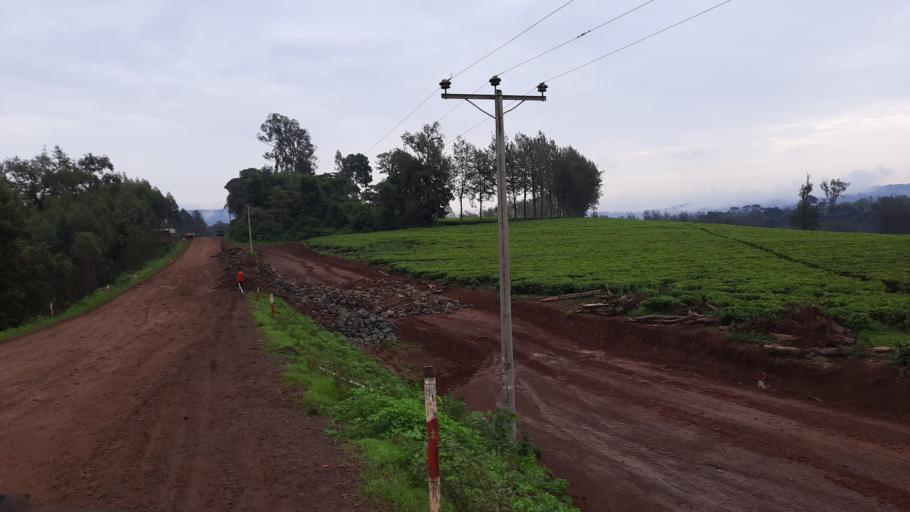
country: ET
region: Oromiya
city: Gore
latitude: 7.8394
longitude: 35.4744
